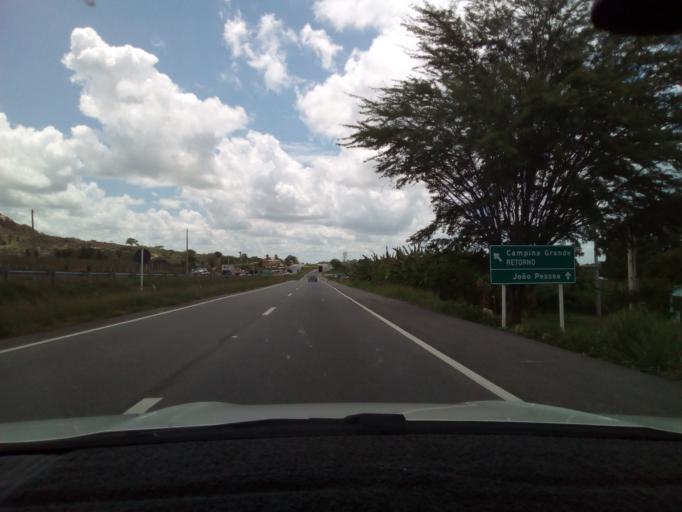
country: BR
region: Paraiba
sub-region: Gurinhem
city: Gurinhem
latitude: -7.1752
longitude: -35.4046
